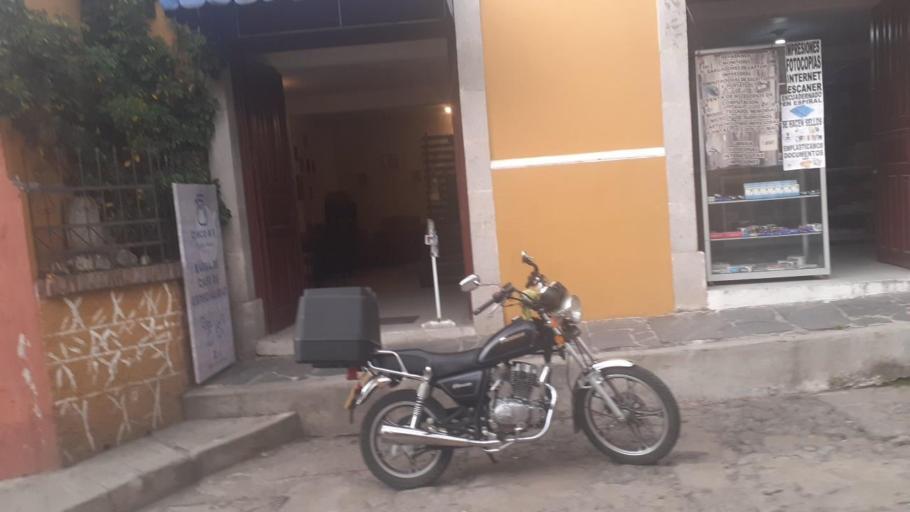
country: GT
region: Quetzaltenango
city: Quetzaltenango
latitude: 14.8375
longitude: -91.5200
